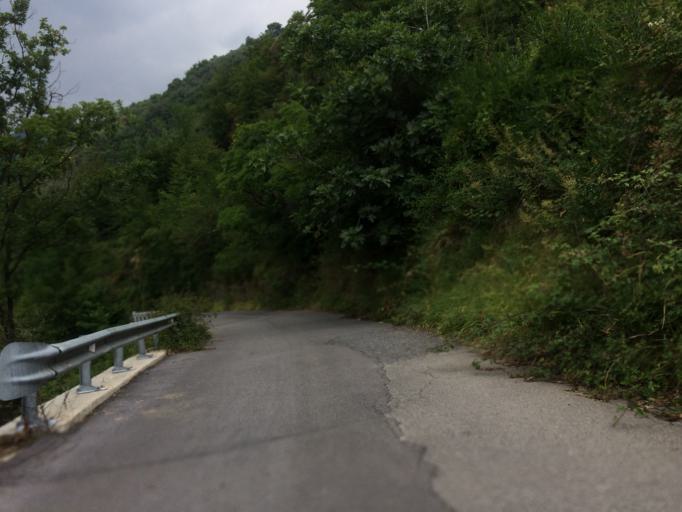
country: IT
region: Liguria
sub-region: Provincia di Imperia
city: Castel Vittorio
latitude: 43.9376
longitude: 7.6852
